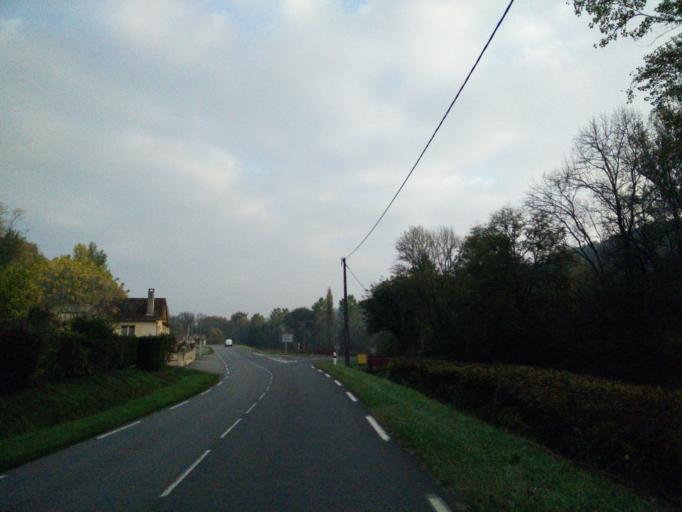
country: FR
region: Aquitaine
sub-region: Departement de la Dordogne
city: Rouffignac-Saint-Cernin-de-Reilhac
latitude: 44.9935
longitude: 0.9447
